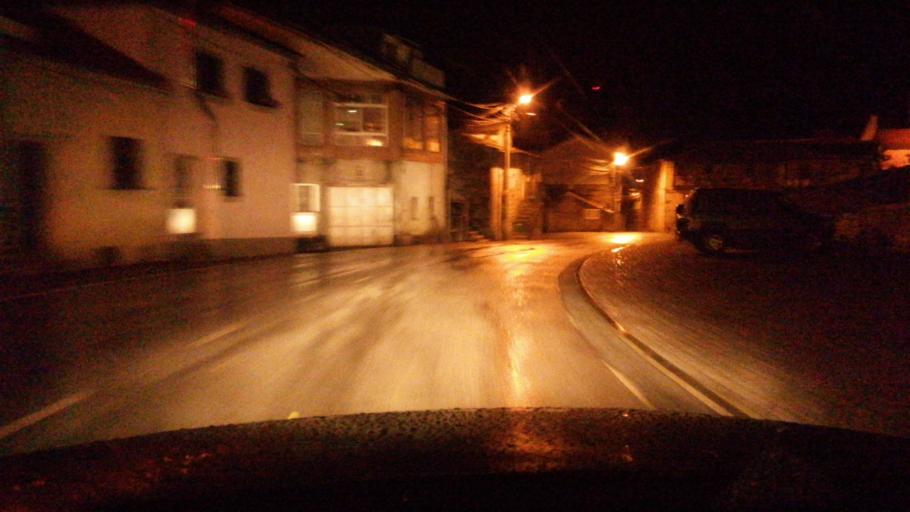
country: PT
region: Viseu
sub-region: Armamar
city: Armamar
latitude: 41.0793
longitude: -7.6691
